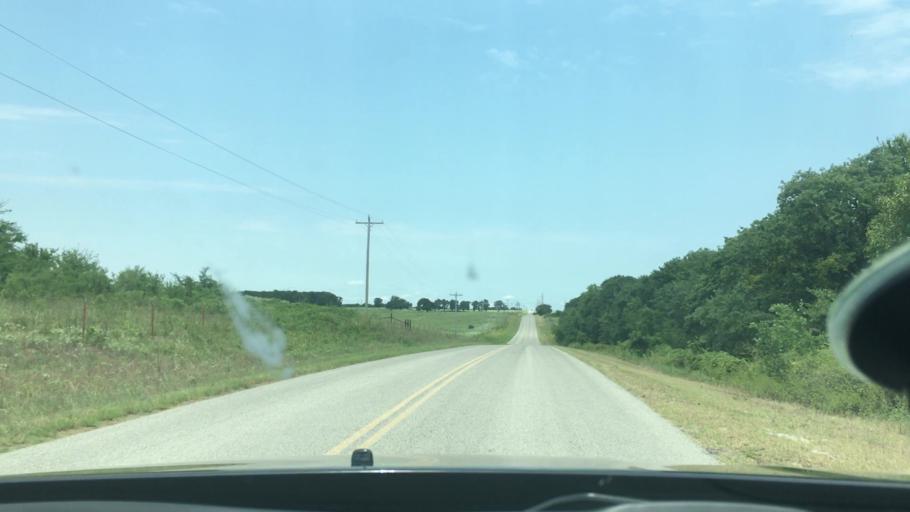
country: US
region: Oklahoma
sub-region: Love County
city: Marietta
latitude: 33.9031
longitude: -97.3521
